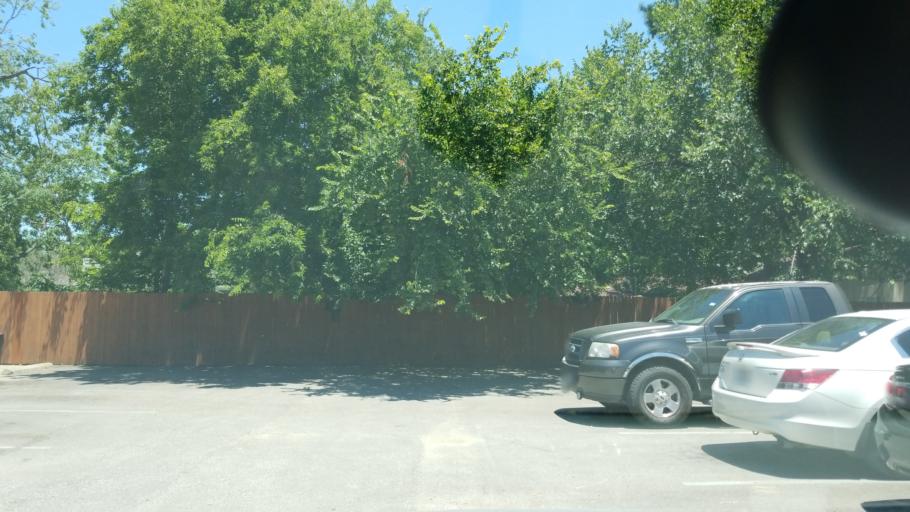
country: US
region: Texas
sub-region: Dallas County
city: Irving
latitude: 32.8243
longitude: -96.9335
